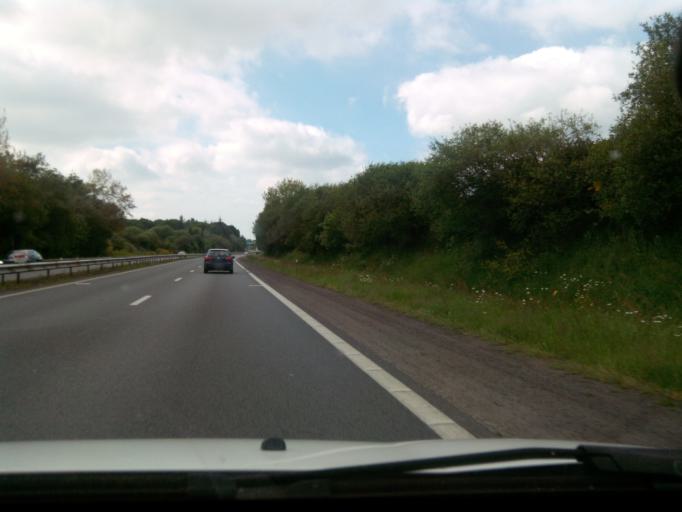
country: FR
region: Brittany
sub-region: Departement des Cotes-d'Armor
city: Plenee-Jugon
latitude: 48.3989
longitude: -2.4063
